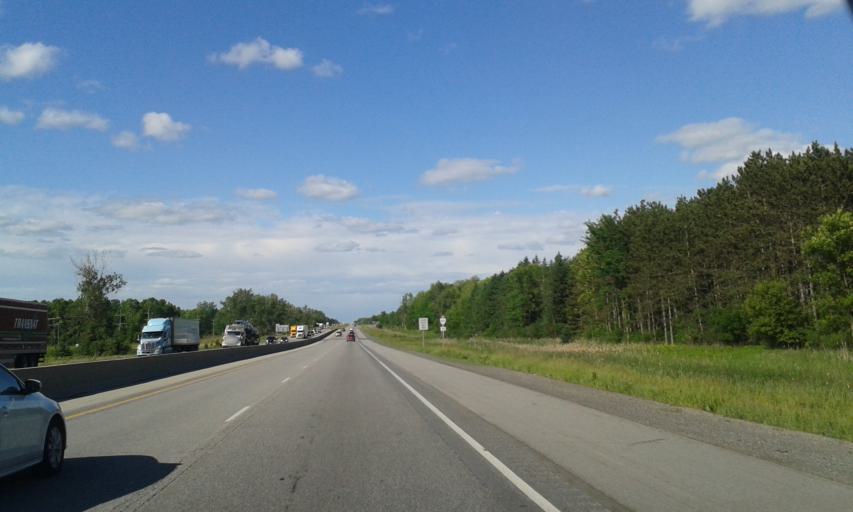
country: CA
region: Ontario
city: Brockville
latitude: 44.6561
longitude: -75.6219
